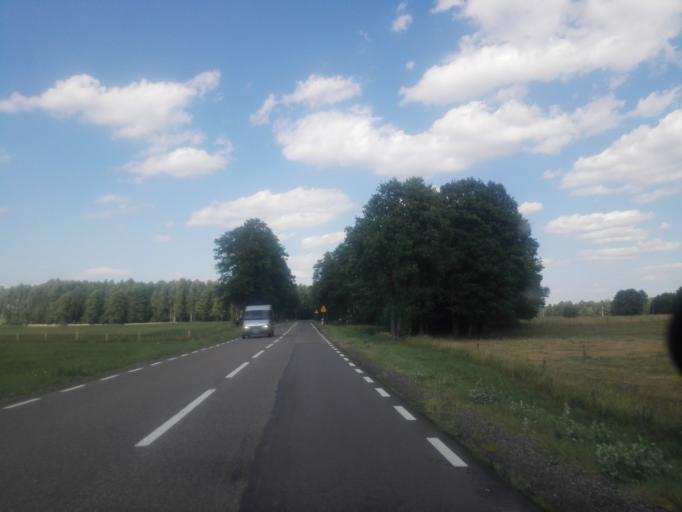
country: PL
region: Podlasie
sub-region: Powiat sejnenski
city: Krasnopol
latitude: 53.9424
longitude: 23.1849
